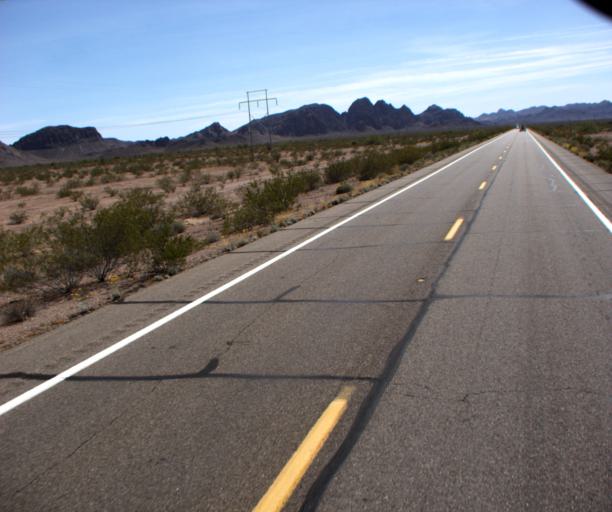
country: US
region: Arizona
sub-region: La Paz County
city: Quartzsite
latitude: 33.3229
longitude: -114.2170
